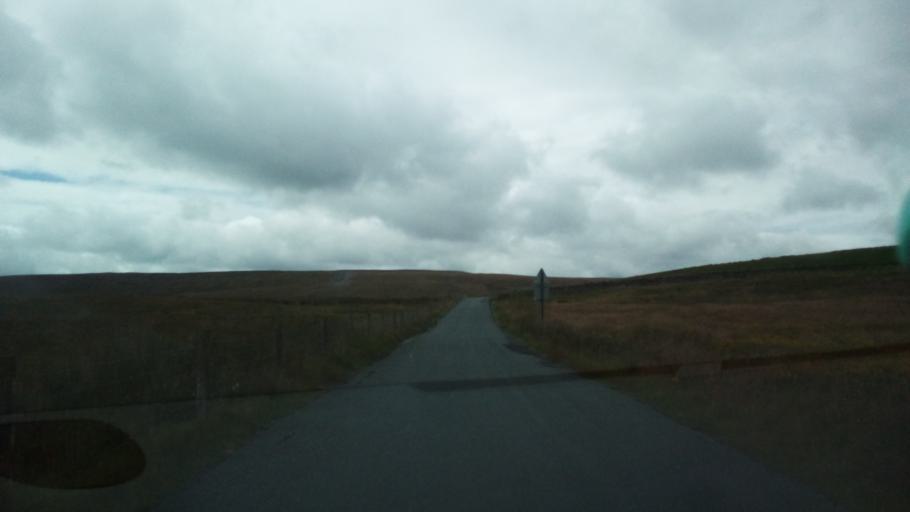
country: GB
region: England
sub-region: North Yorkshire
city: Ingleton
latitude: 54.2474
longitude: -2.3168
